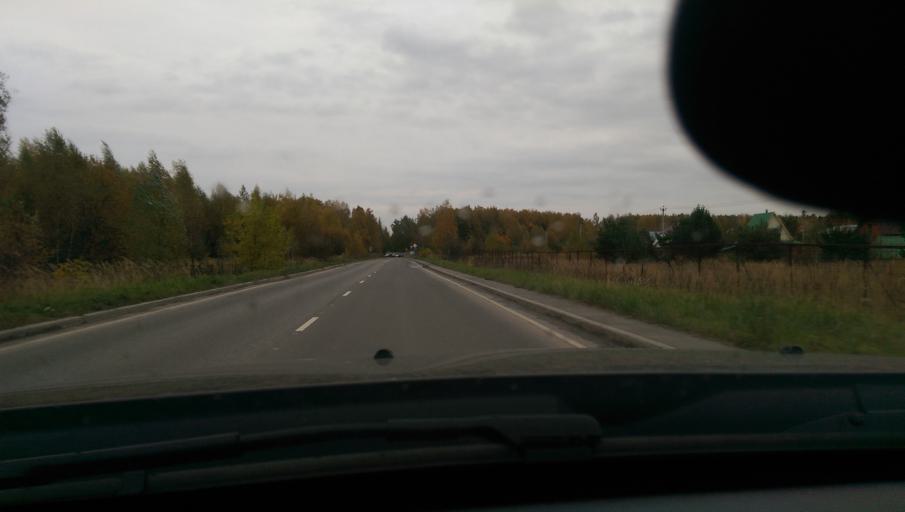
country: RU
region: Moskovskaya
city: Pirogovskiy
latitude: 56.0183
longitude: 37.7260
